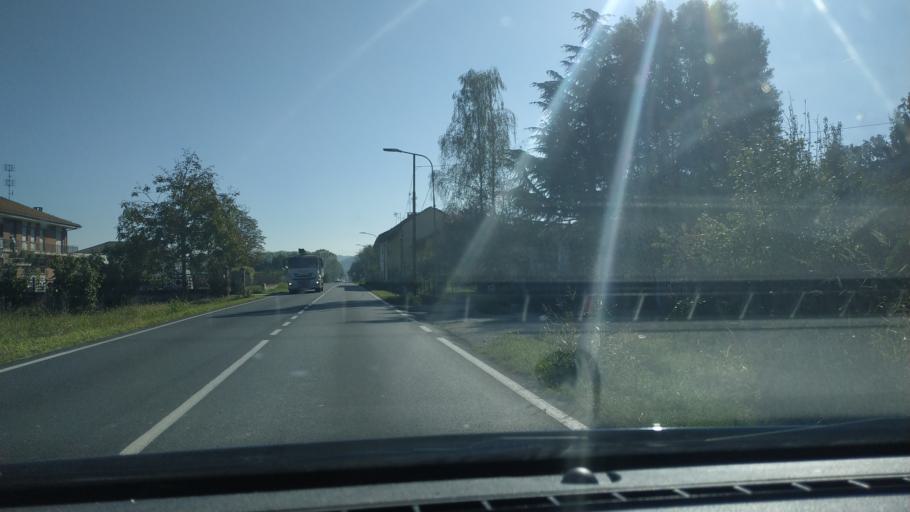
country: IT
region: Piedmont
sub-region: Provincia di Torino
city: Pomaretto
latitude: 45.1582
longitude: 8.0337
